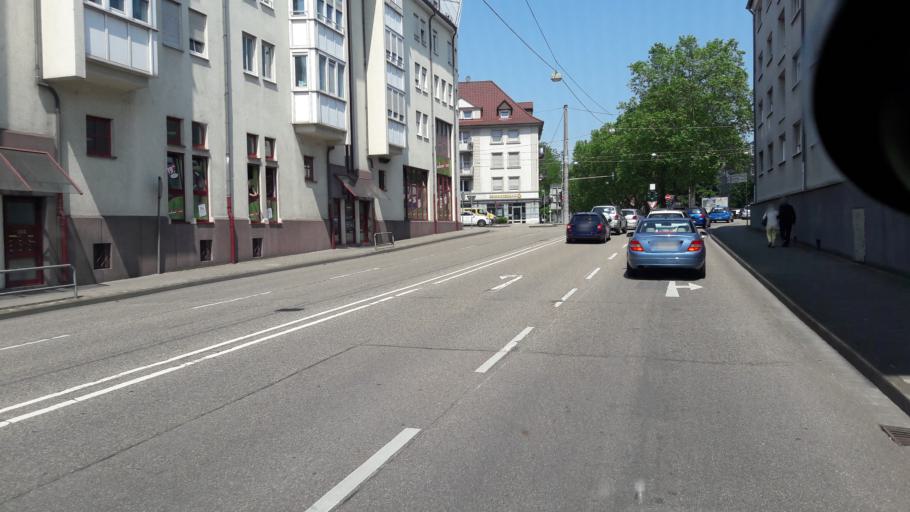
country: DE
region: Baden-Wuerttemberg
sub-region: Karlsruhe Region
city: Rastatt
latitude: 48.8583
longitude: 8.2105
